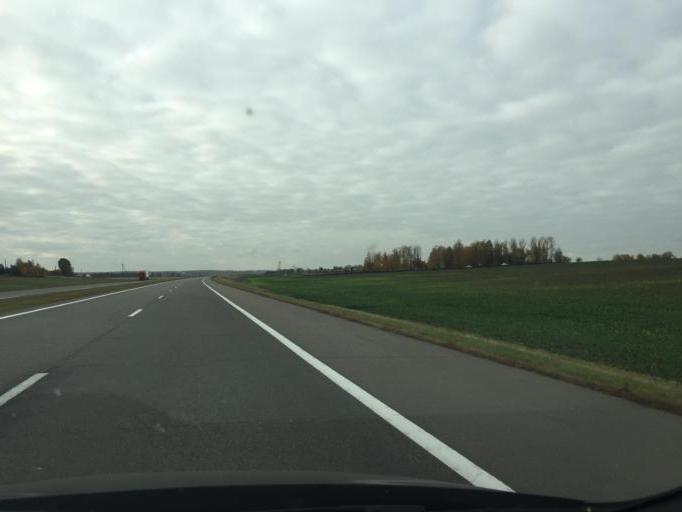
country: BY
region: Minsk
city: Stan'kava
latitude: 53.6778
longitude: 27.2655
